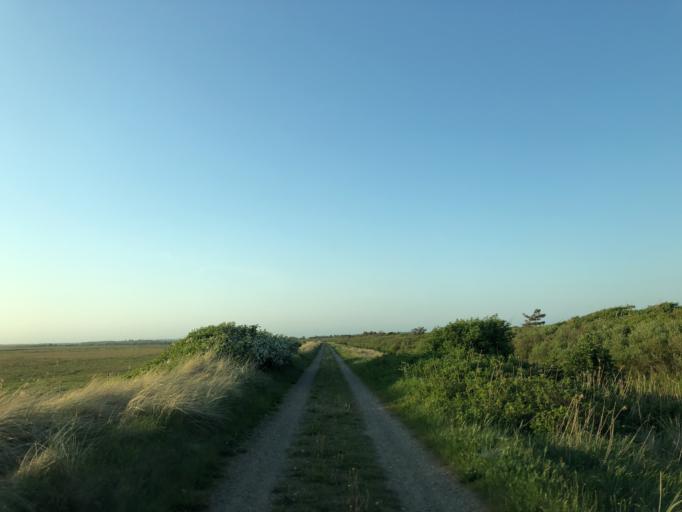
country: DK
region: Central Jutland
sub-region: Holstebro Kommune
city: Ulfborg
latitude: 56.2318
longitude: 8.1662
